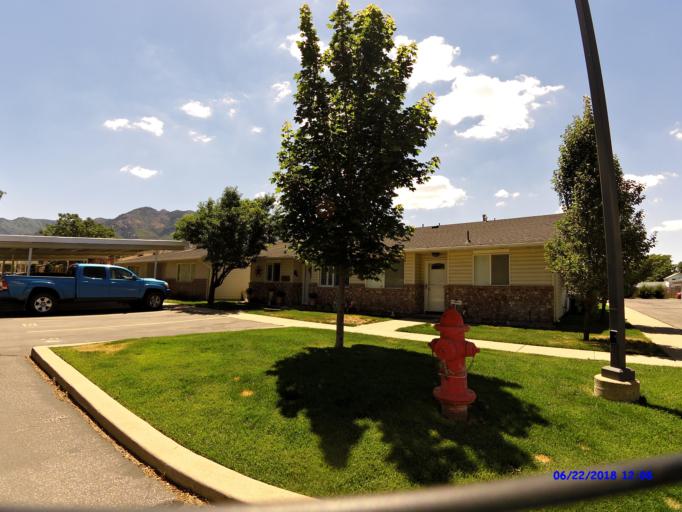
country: US
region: Utah
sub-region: Weber County
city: Ogden
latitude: 41.2404
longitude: -111.9561
